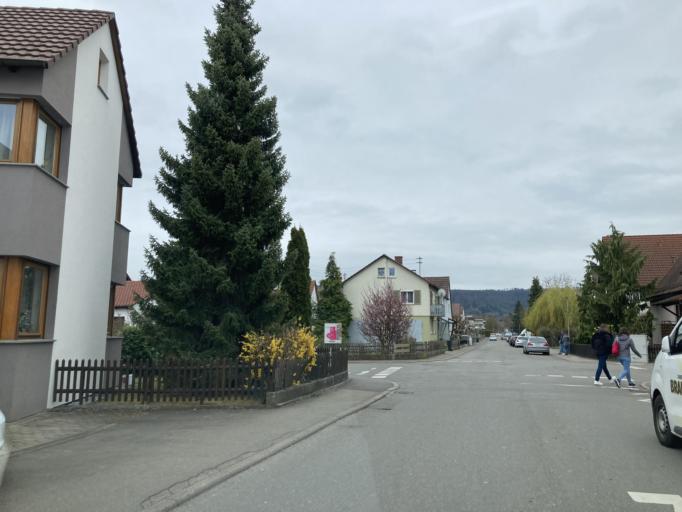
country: DE
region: Baden-Wuerttemberg
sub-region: Tuebingen Region
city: Rottenburg
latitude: 48.4779
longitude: 8.9460
